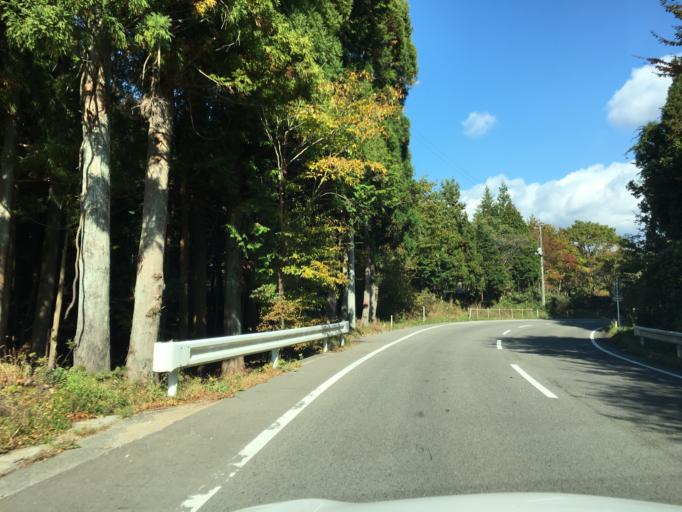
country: JP
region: Fukushima
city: Funehikimachi-funehiki
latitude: 37.2985
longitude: 140.7594
